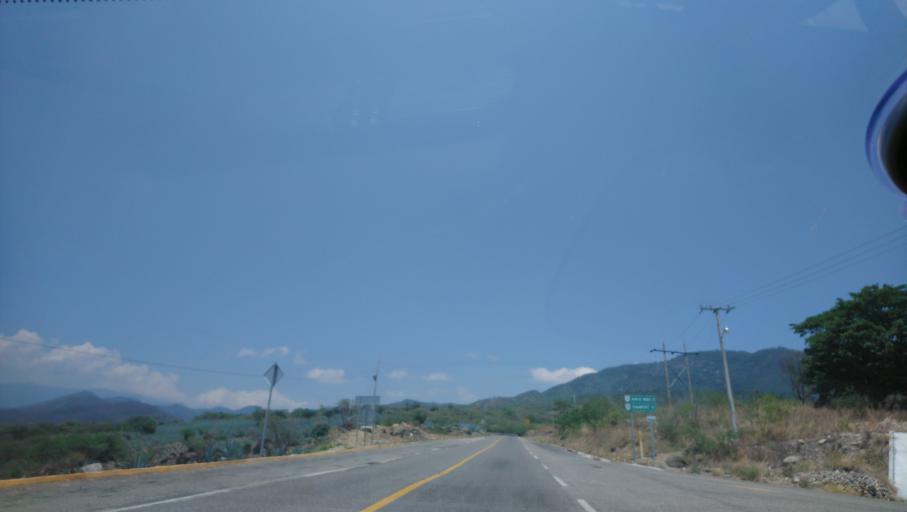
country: MX
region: Oaxaca
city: San Carlos Yautepec
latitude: 16.5623
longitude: -96.0206
